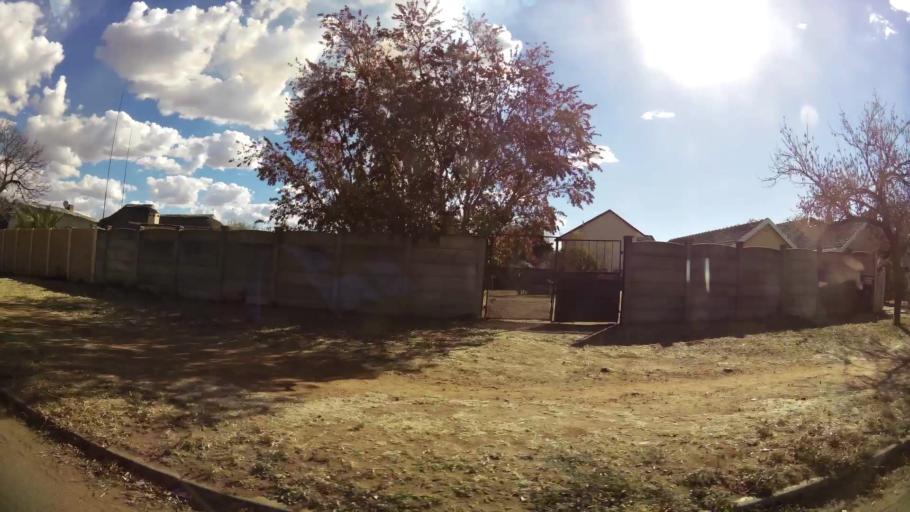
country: ZA
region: North-West
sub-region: Dr Kenneth Kaunda District Municipality
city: Klerksdorp
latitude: -26.8411
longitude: 26.6532
